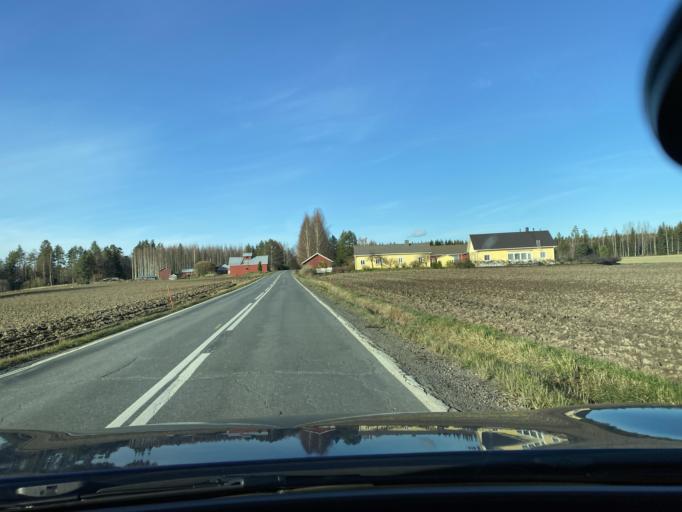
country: FI
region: Haeme
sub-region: Forssa
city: Tammela
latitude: 60.8353
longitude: 23.8386
